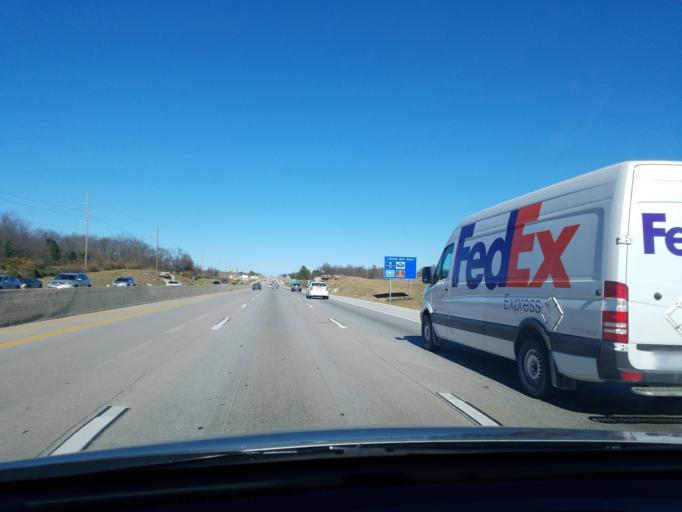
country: US
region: Missouri
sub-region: Greene County
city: Springfield
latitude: 37.1406
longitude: -93.2246
